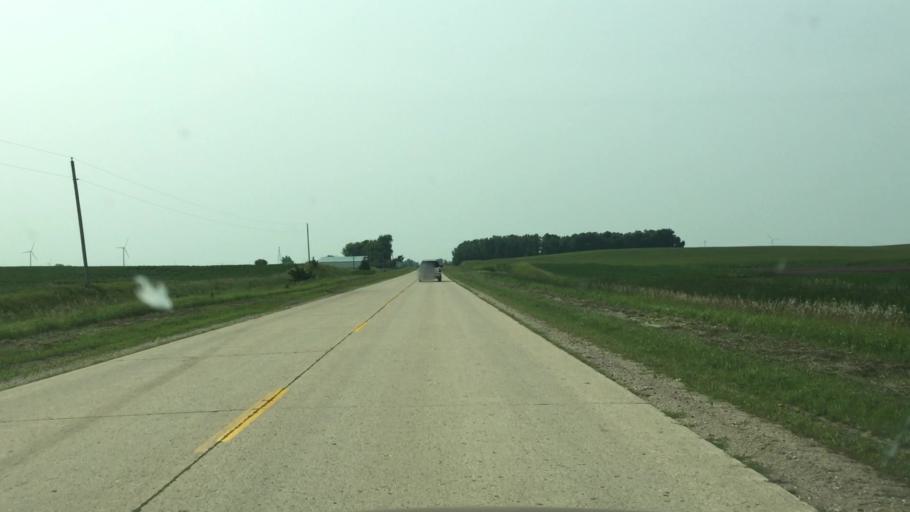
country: US
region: Iowa
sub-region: Dickinson County
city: Lake Park
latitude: 43.4251
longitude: -95.2891
